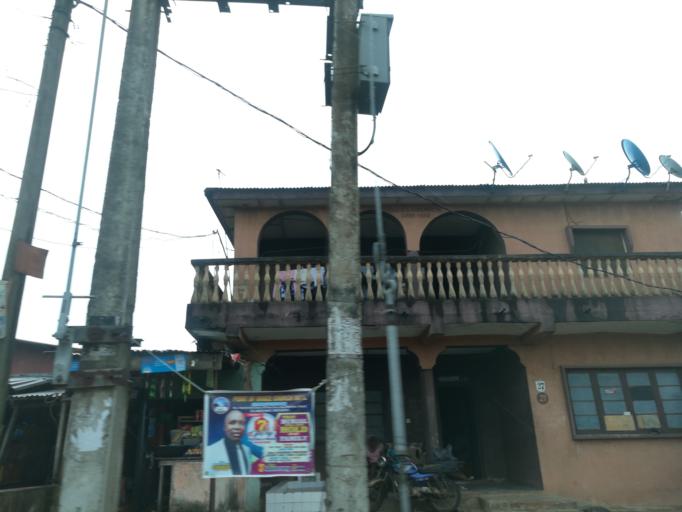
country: NG
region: Lagos
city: Oshodi
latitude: 6.5583
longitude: 3.3375
